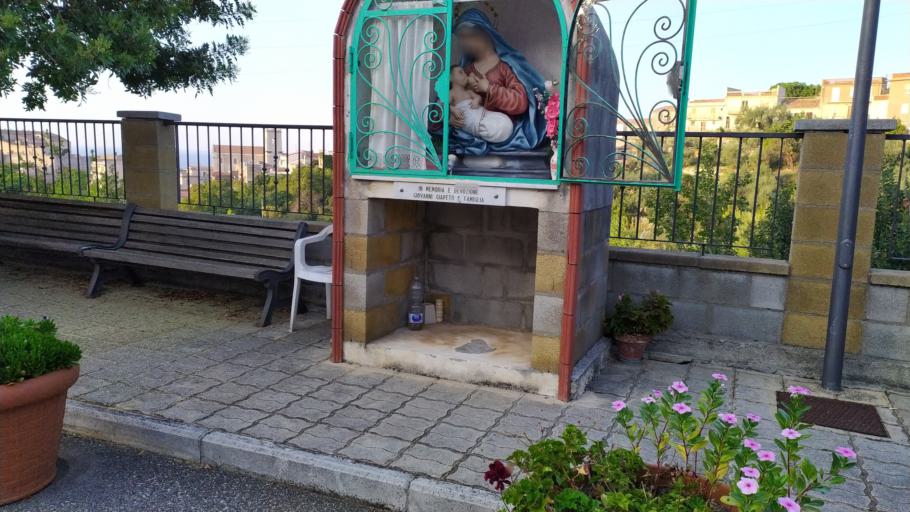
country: IT
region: Sicily
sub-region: Messina
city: Saponara Marittima
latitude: 38.2293
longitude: 15.4362
